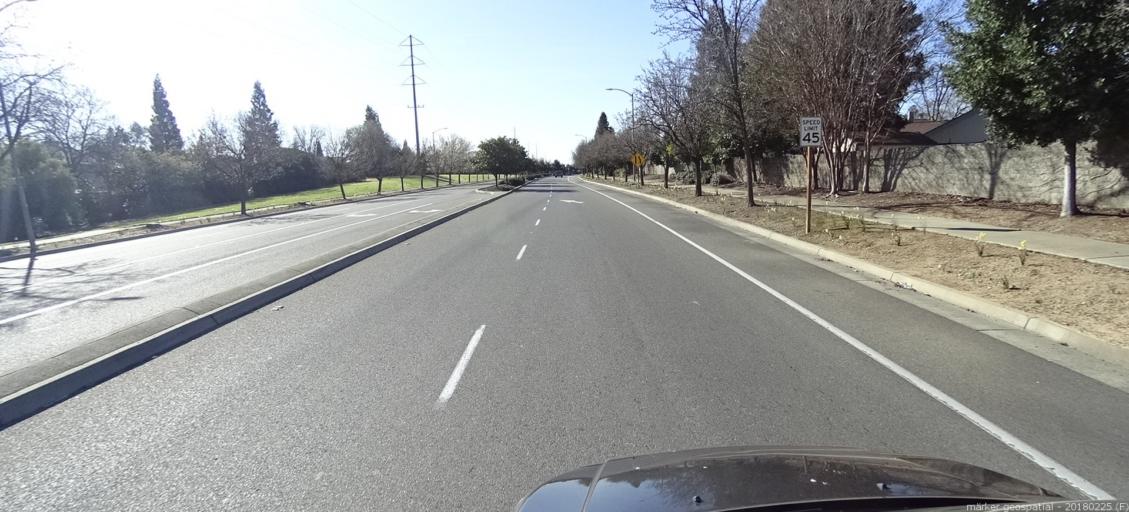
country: US
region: California
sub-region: Sacramento County
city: Antelope
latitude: 38.7181
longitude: -121.3467
